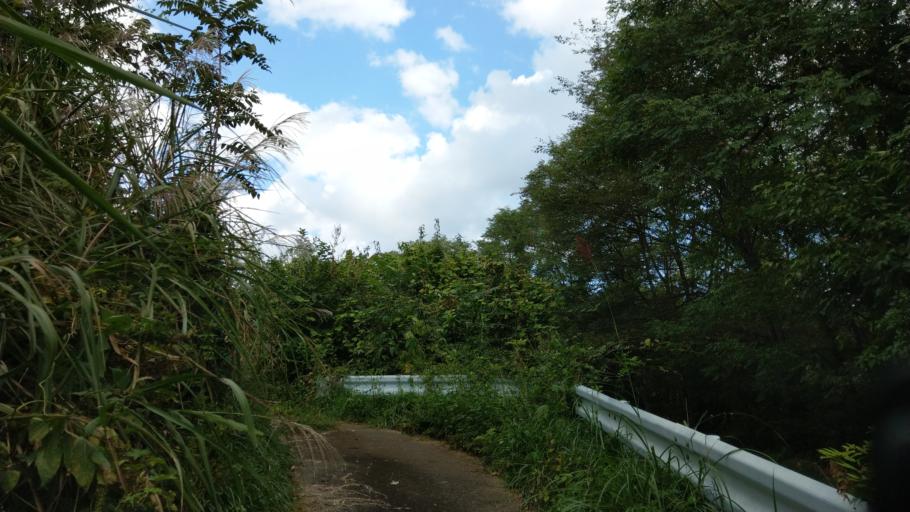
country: JP
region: Nagano
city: Komoro
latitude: 36.3491
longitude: 138.4169
